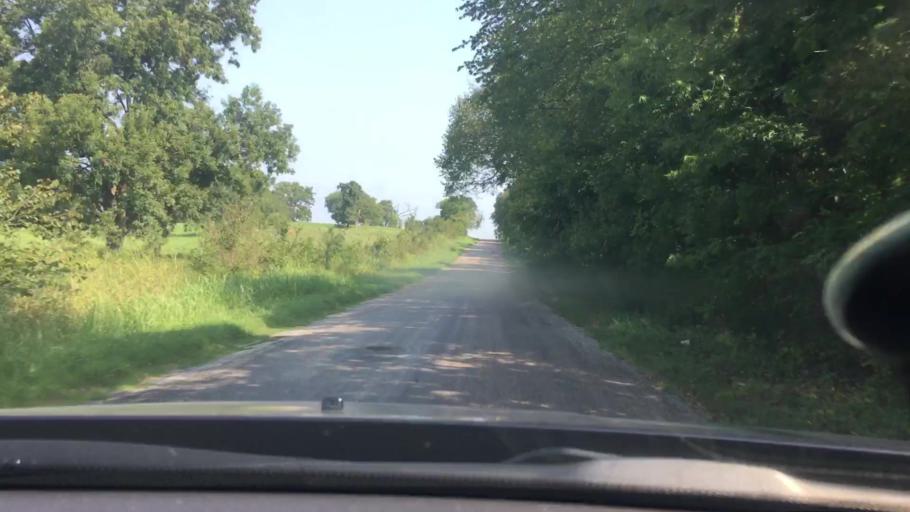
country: US
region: Oklahoma
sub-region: Pontotoc County
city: Ada
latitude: 34.6626
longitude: -96.5298
